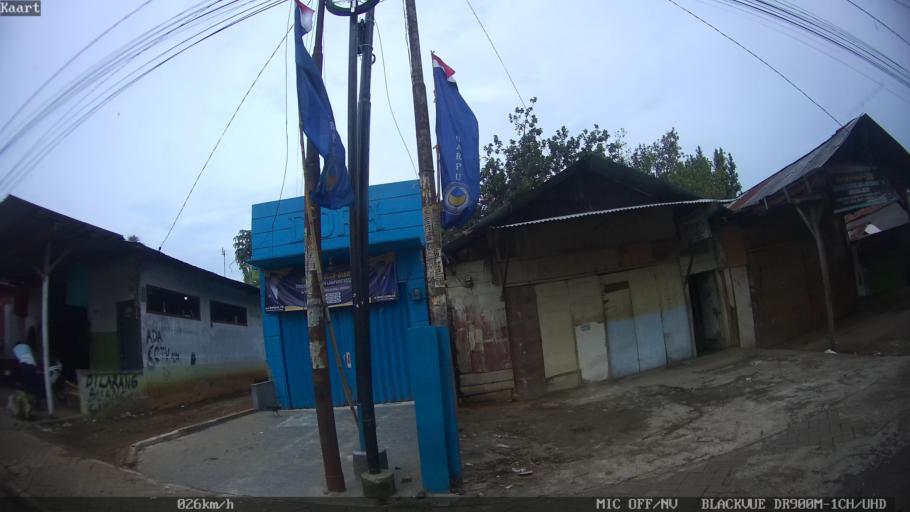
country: ID
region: Lampung
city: Kedaton
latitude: -5.3913
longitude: 105.2151
